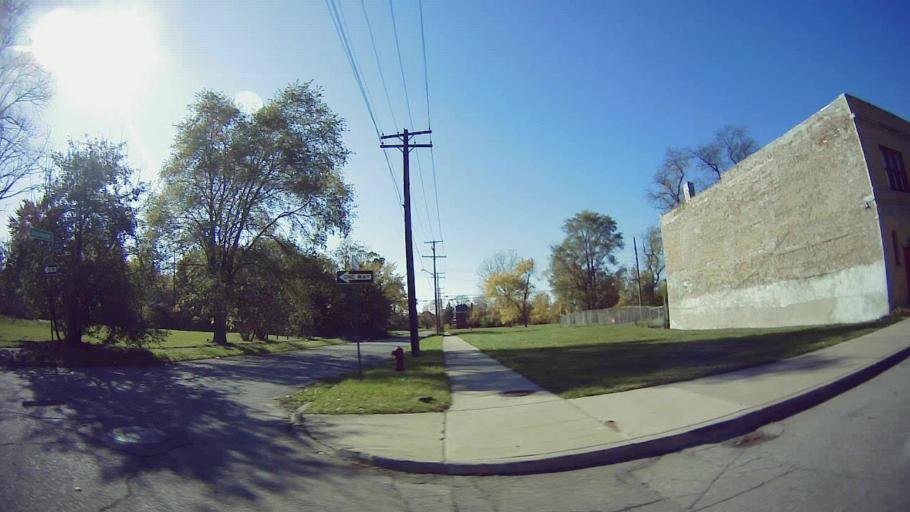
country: US
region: Michigan
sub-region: Wayne County
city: Highland Park
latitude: 42.3568
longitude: -83.0910
